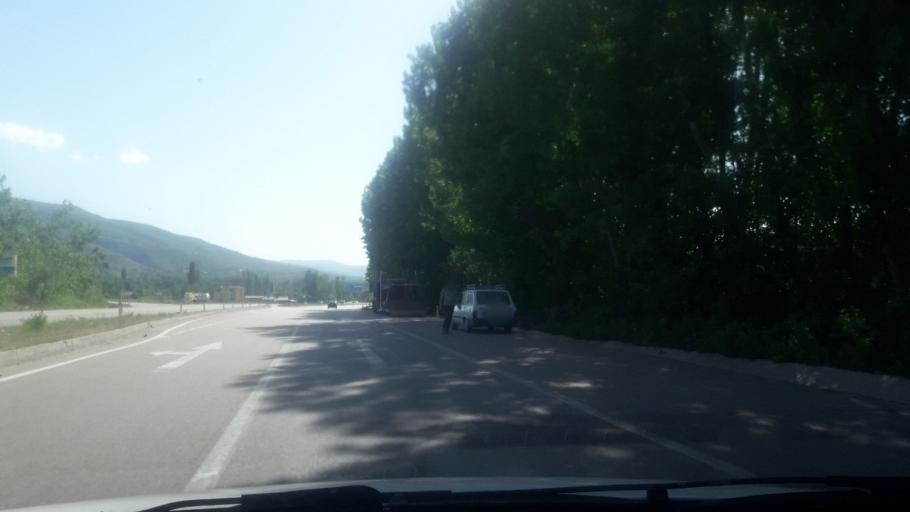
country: TR
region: Tokat
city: Yesilyurt
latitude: 40.3008
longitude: 36.3723
